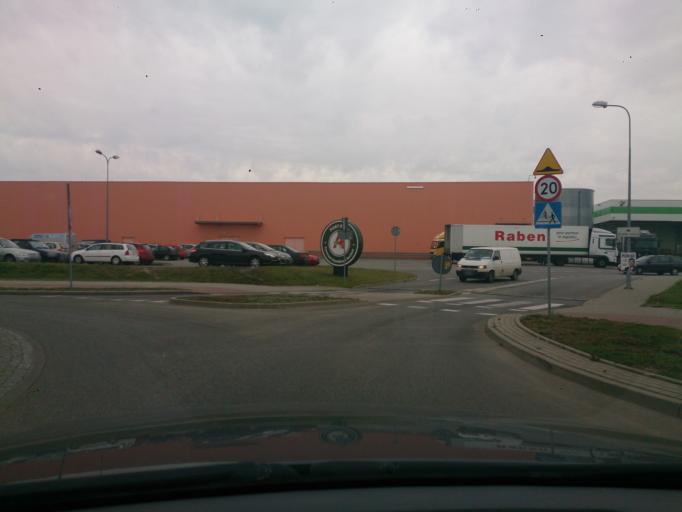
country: PL
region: Pomeranian Voivodeship
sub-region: Powiat wejherowski
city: Rumia
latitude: 54.5880
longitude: 18.3726
